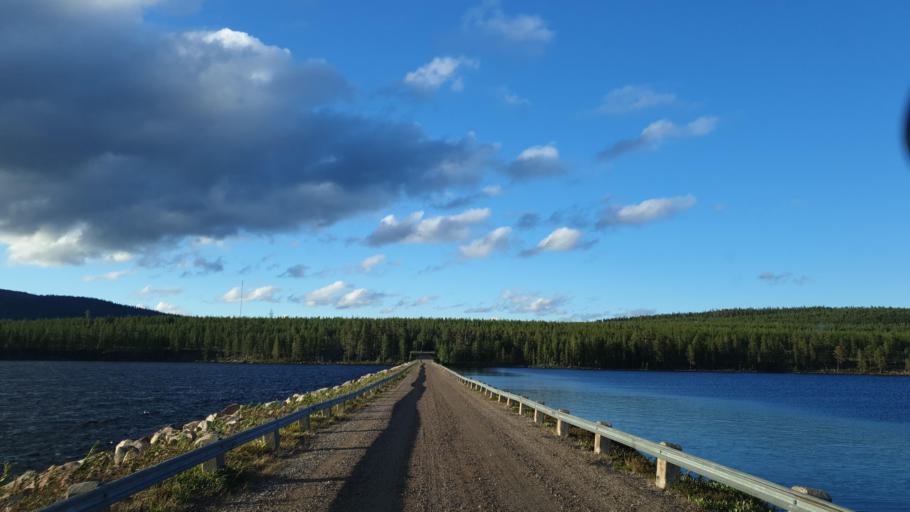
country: SE
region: Norrbotten
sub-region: Arvidsjaurs Kommun
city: Arvidsjaur
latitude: 65.7106
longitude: 18.7077
